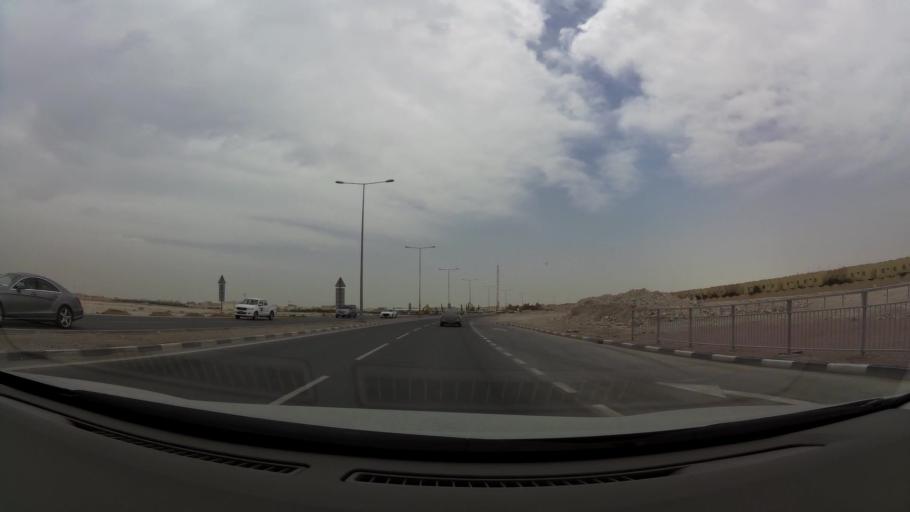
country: QA
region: Baladiyat ad Dawhah
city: Doha
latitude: 25.2344
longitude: 51.4703
